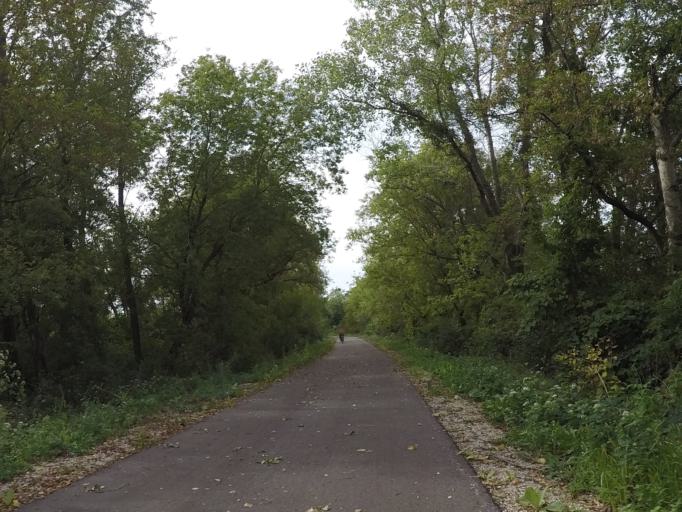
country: US
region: Wisconsin
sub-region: Sauk County
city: Prairie du Sac
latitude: 43.3335
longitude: -89.7502
